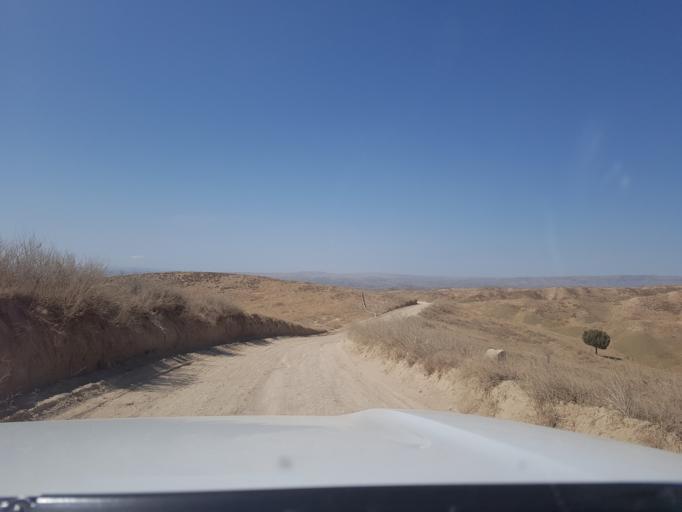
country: TM
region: Ahal
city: Baharly
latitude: 38.2678
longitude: 56.8911
